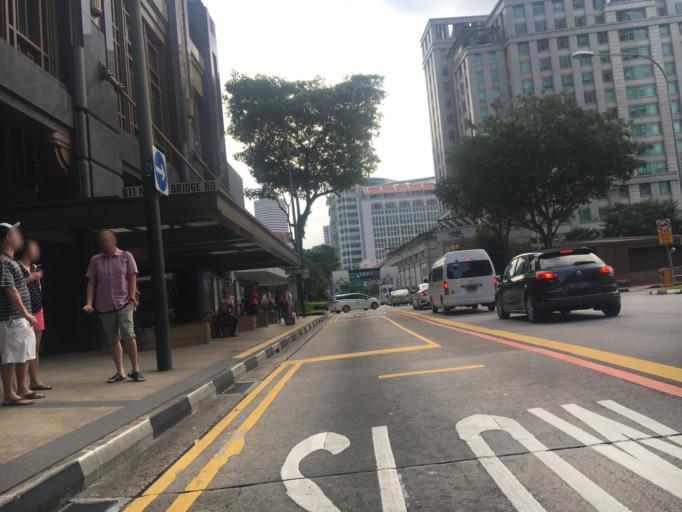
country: SG
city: Singapore
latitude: 1.3006
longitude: 103.8574
